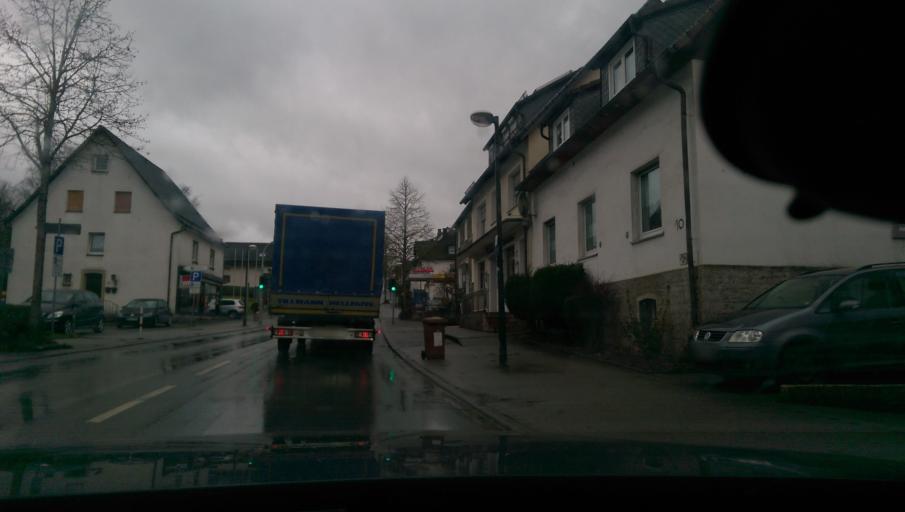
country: DE
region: North Rhine-Westphalia
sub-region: Regierungsbezirk Arnsberg
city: Sundern
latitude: 51.3187
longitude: 8.0066
